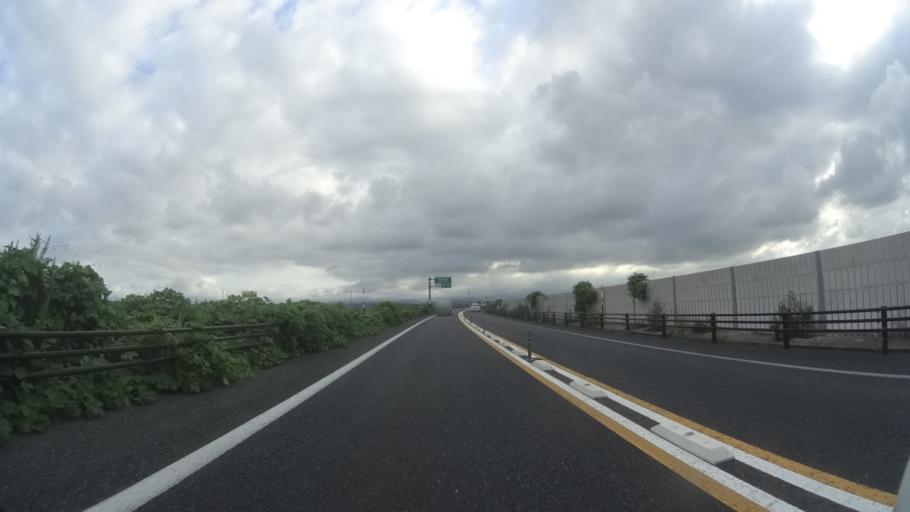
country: JP
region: Tottori
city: Kurayoshi
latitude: 35.4905
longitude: 133.7080
